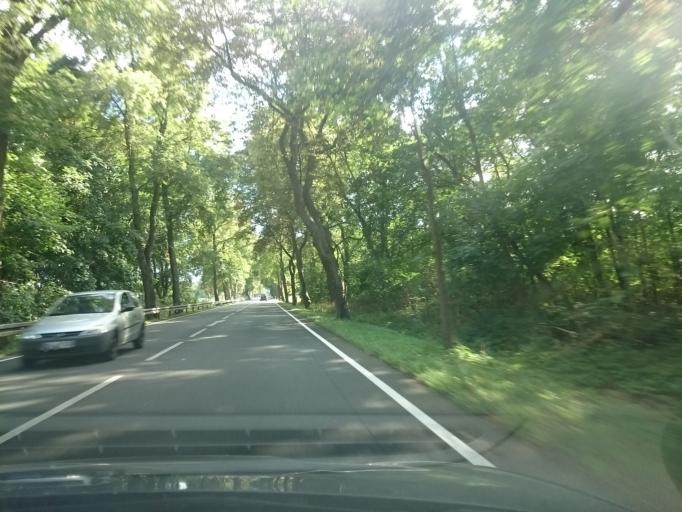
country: DE
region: Mecklenburg-Vorpommern
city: Neustrelitz
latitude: 53.3147
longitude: 13.0994
